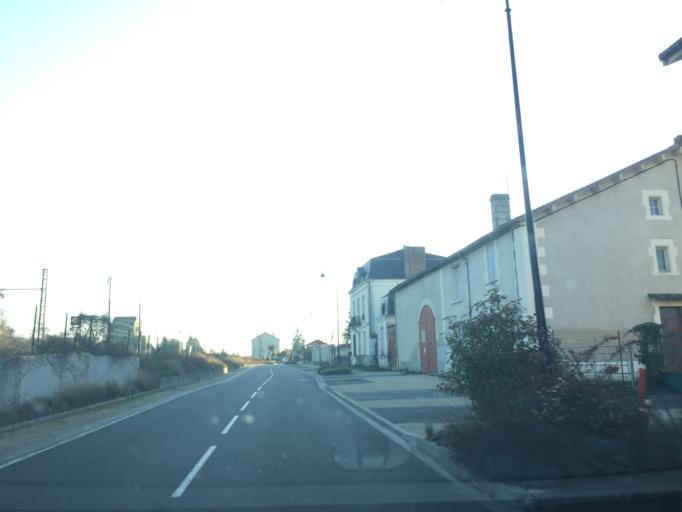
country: FR
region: Poitou-Charentes
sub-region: Departement de la Charente
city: Chalais
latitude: 45.2701
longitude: 0.0428
